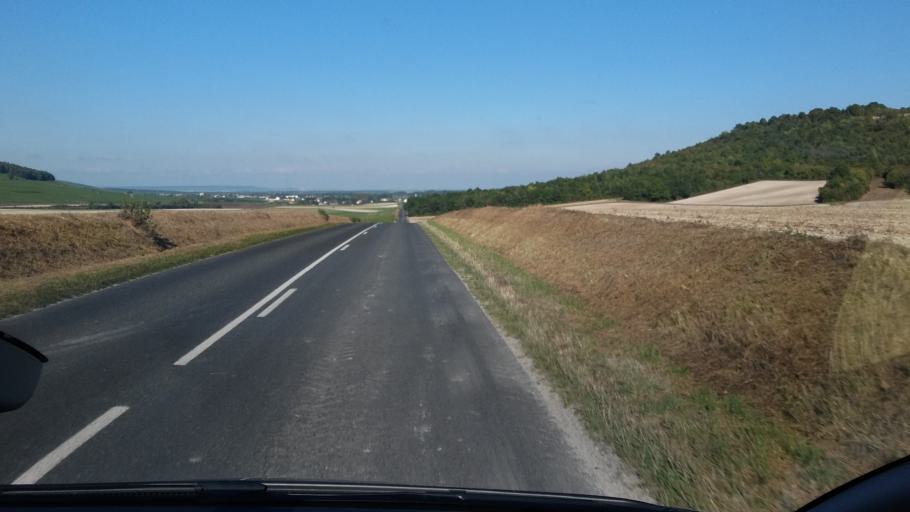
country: FR
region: Champagne-Ardenne
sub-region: Departement de la Marne
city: Vertus
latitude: 48.8588
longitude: 3.9792
